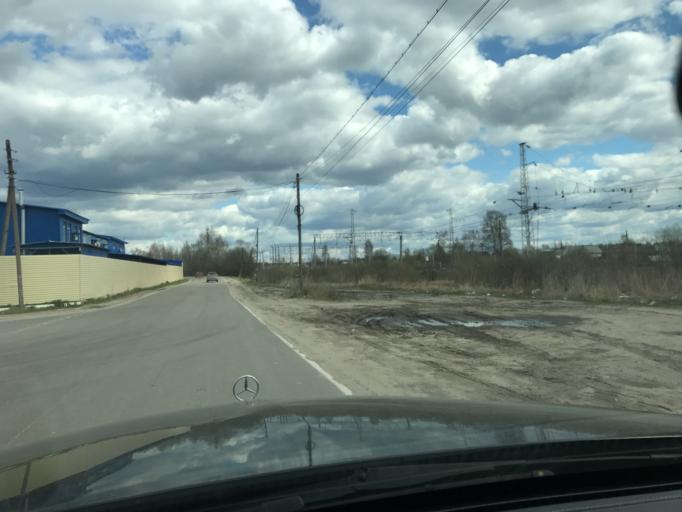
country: RU
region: Vladimir
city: Pokrov
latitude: 55.8889
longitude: 39.2066
